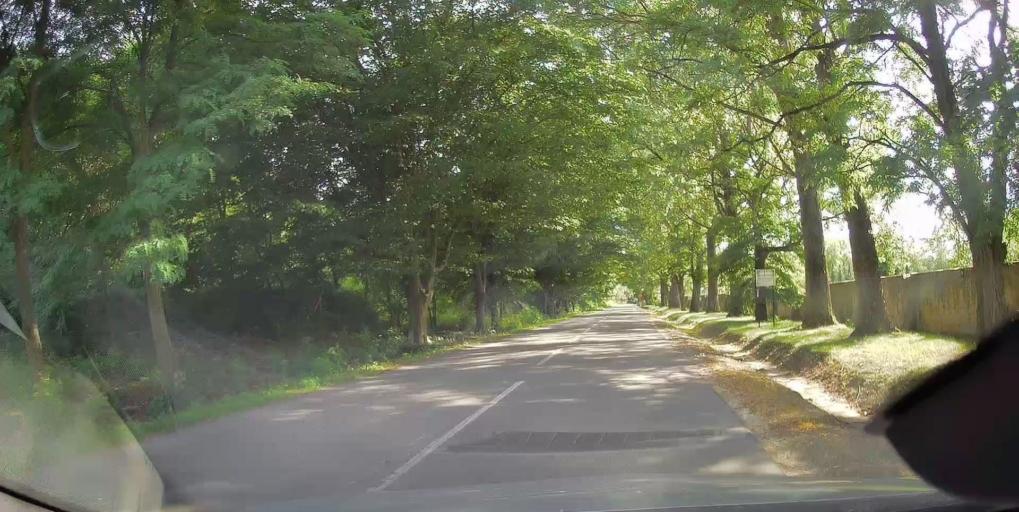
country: PL
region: Lodz Voivodeship
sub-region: Powiat opoczynski
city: Mniszkow
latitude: 51.4113
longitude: 20.0485
